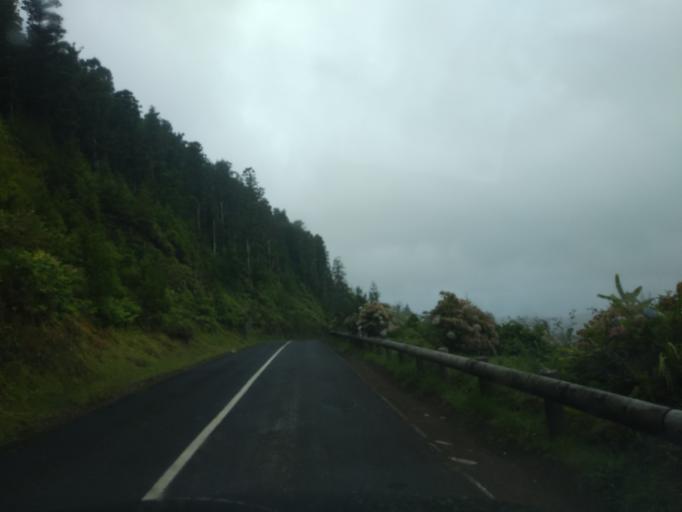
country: PT
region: Azores
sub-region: Ponta Delgada
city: Arrifes
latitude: 37.8372
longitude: -25.7857
